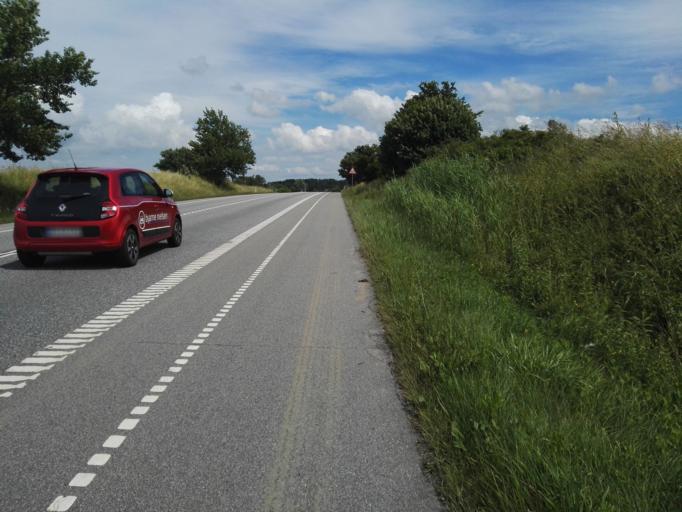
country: DK
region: Capital Region
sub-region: Frederikssund Kommune
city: Slangerup
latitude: 55.8675
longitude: 12.1820
